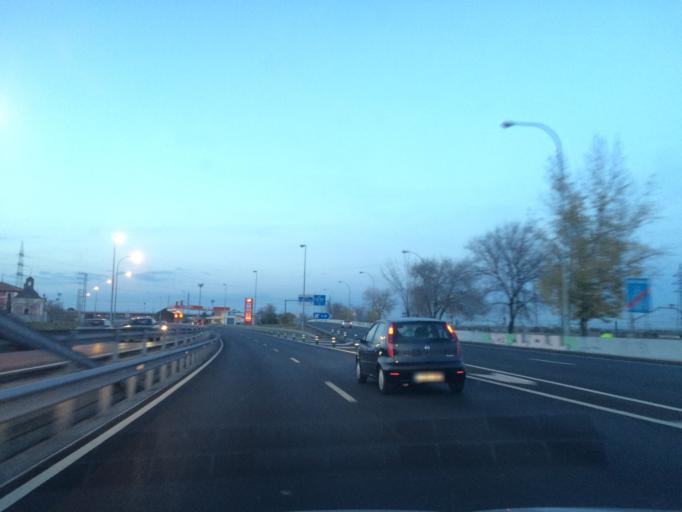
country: ES
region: Madrid
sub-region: Provincia de Madrid
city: Las Tablas
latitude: 40.5142
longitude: -3.6847
